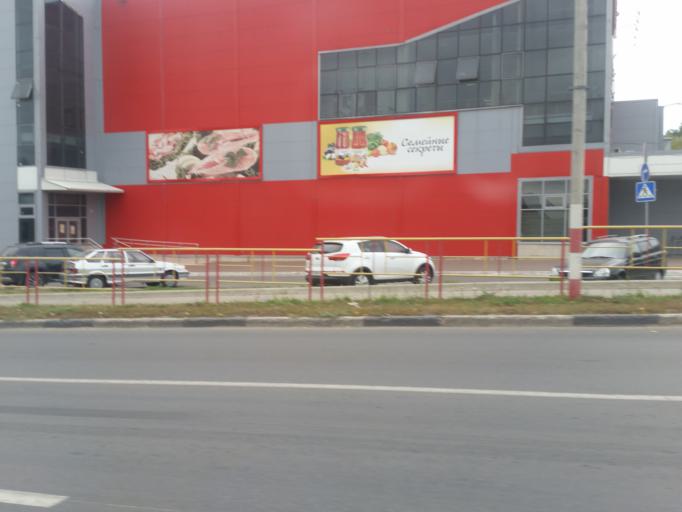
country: RU
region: Ulyanovsk
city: Dimitrovgrad
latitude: 54.2258
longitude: 49.5676
